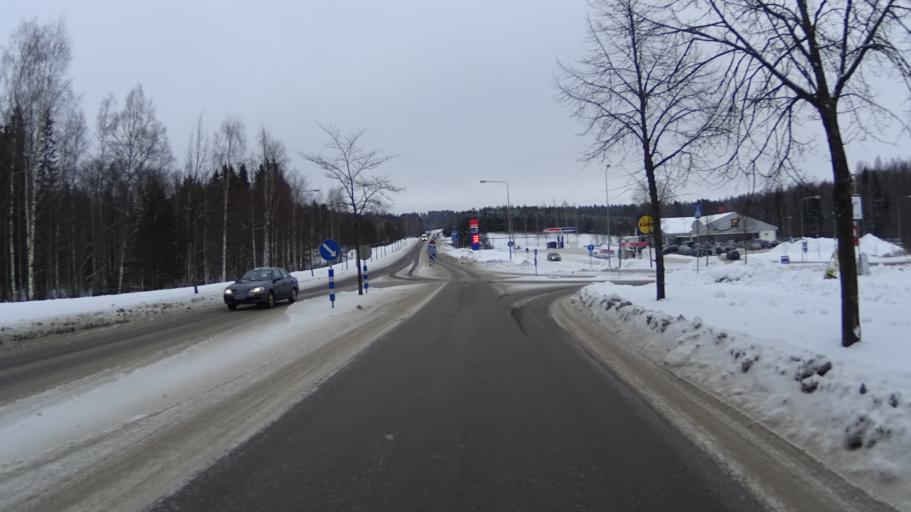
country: FI
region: Uusimaa
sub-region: Helsinki
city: Karkkila
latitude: 60.5336
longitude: 24.2333
